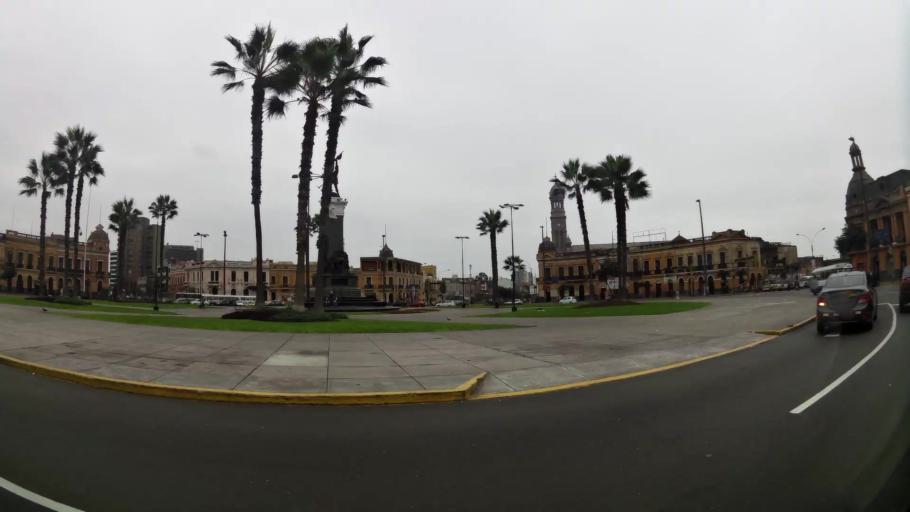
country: PE
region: Lima
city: Lima
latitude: -12.0598
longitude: -77.0414
